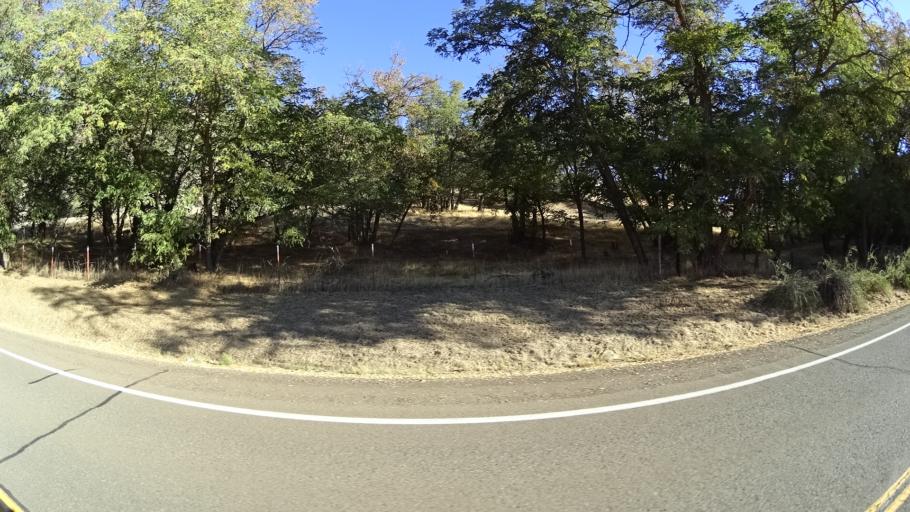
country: US
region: California
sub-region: Siskiyou County
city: Montague
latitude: 41.9004
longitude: -122.5108
